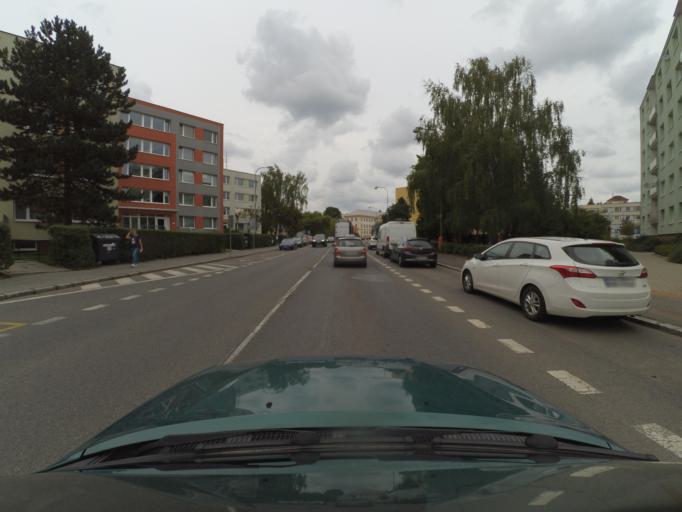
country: CZ
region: Central Bohemia
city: Rakovnik
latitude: 50.1040
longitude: 13.7256
